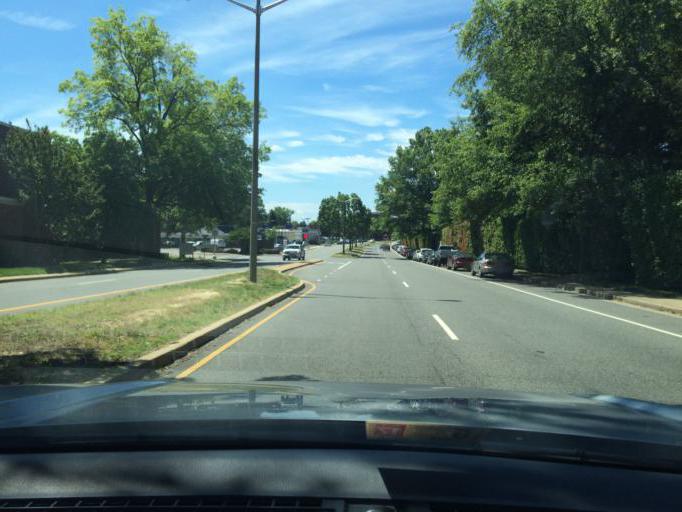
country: US
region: Virginia
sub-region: Fairfax County
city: Huntington
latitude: 38.8329
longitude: -77.0854
